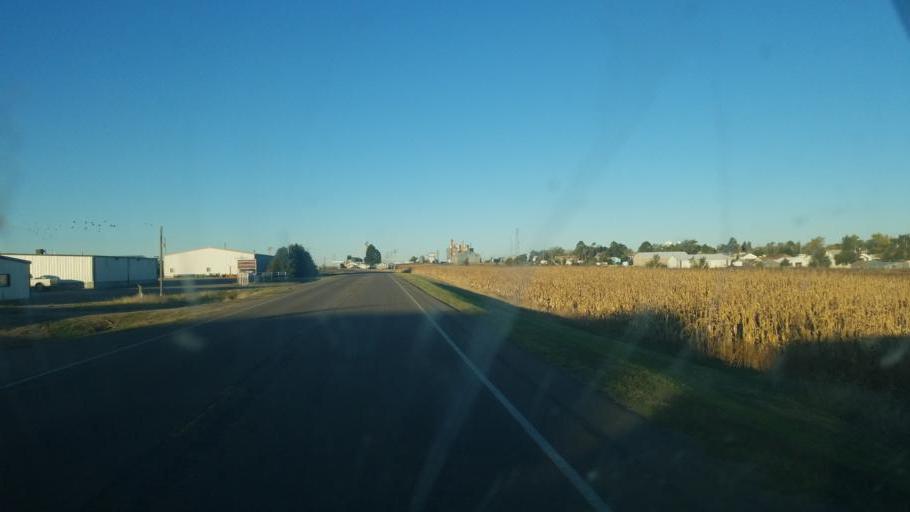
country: US
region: Colorado
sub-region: Cheyenne County
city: Cheyenne Wells
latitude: 38.8214
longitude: -102.3362
